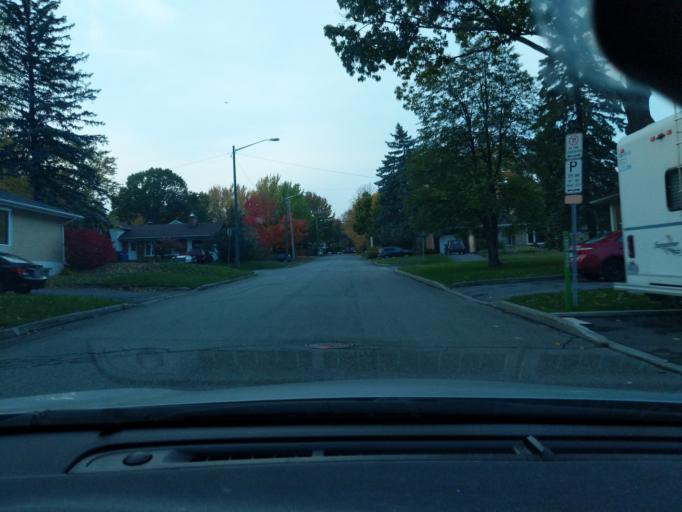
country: CA
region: Quebec
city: Quebec
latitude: 46.7628
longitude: -71.2771
